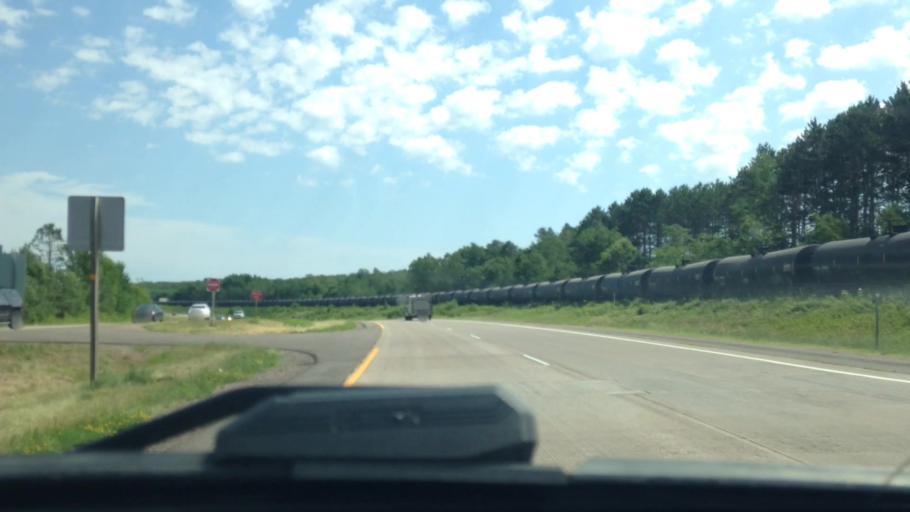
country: US
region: Wisconsin
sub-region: Washburn County
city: Spooner
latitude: 45.8632
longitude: -91.8373
